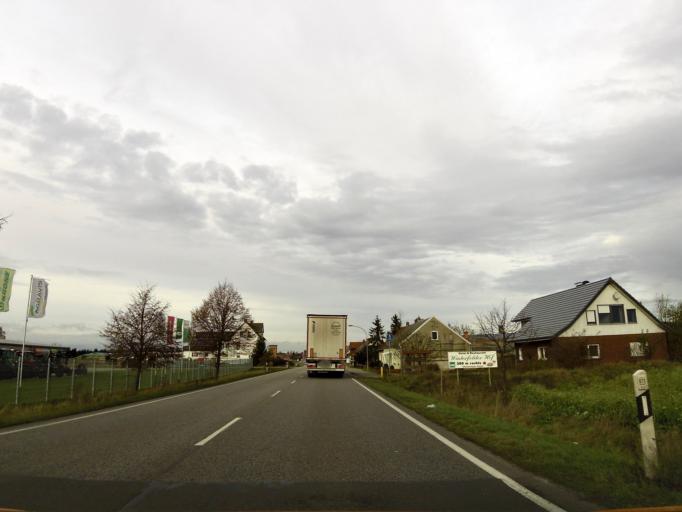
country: DE
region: Saxony-Anhalt
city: Pretzier
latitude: 52.7338
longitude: 11.2452
